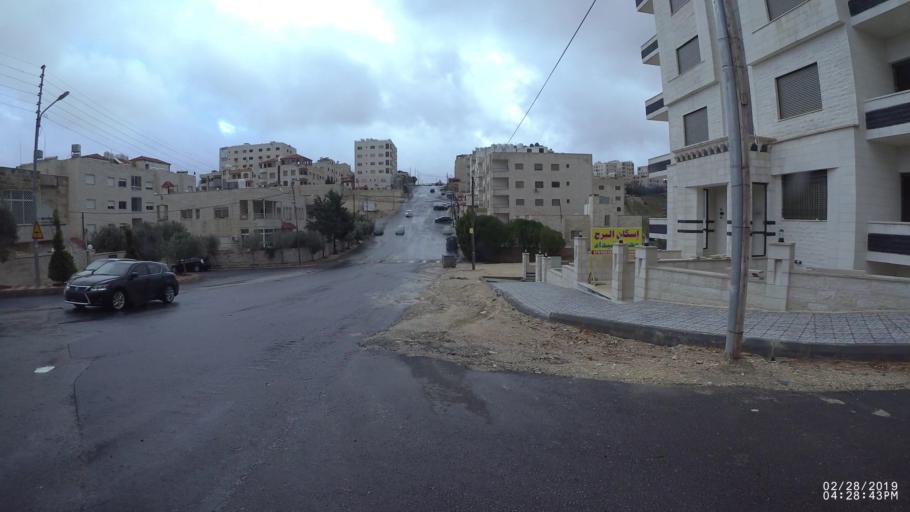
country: JO
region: Amman
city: Amman
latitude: 32.0058
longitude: 35.9290
